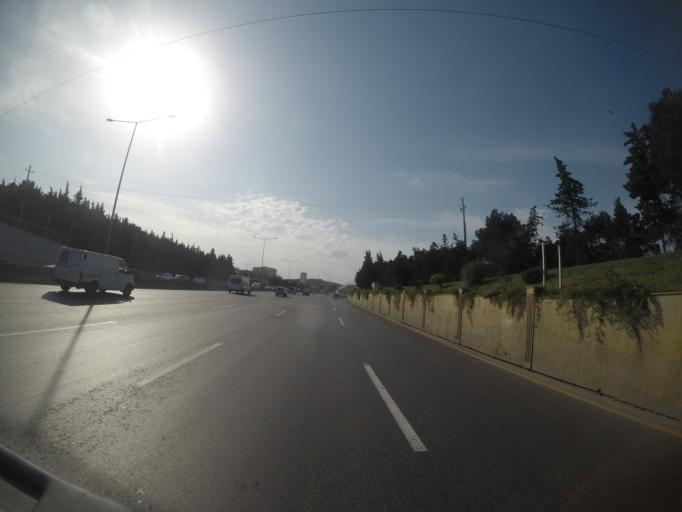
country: AZ
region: Abseron
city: Khirdalan
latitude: 40.4376
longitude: 49.7782
